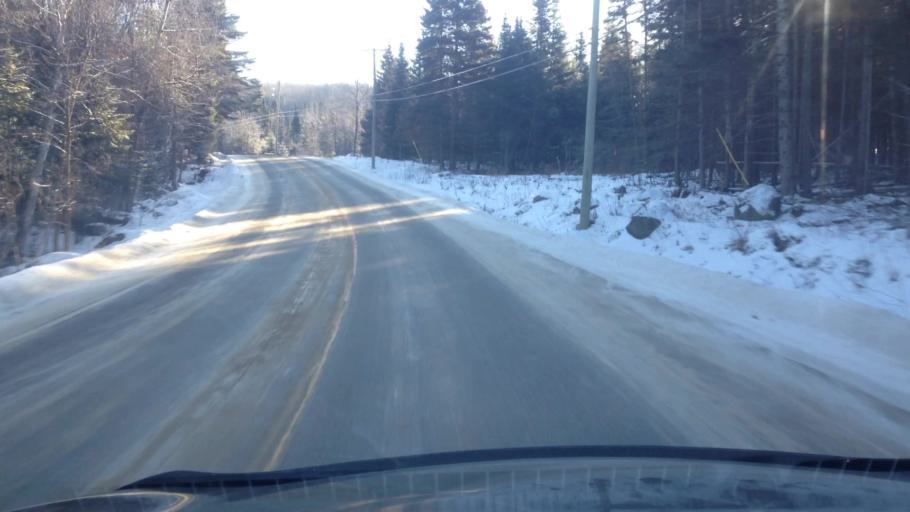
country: CA
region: Quebec
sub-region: Laurentides
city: Brownsburg-Chatham
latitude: 45.9207
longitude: -74.5254
